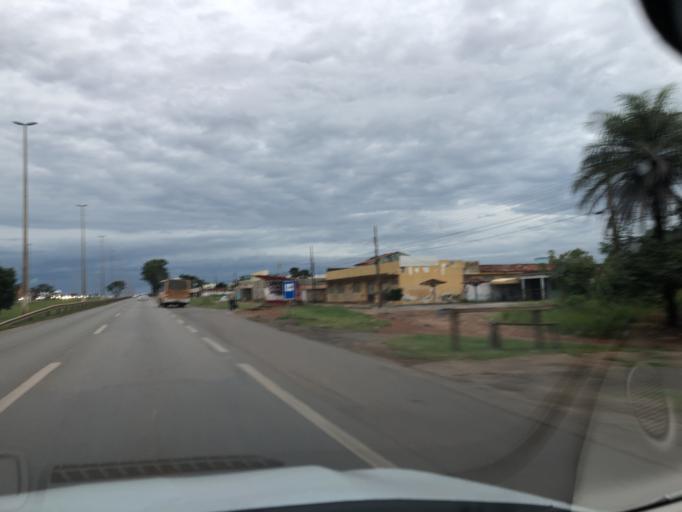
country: BR
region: Goias
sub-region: Luziania
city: Luziania
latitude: -16.1416
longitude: -47.9482
